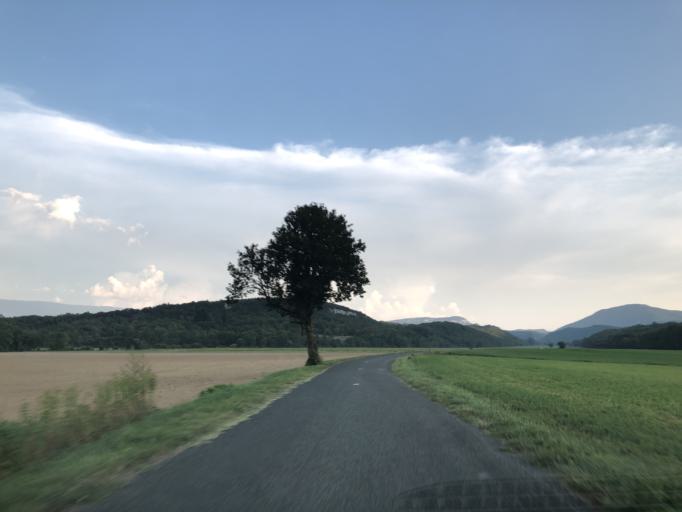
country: FR
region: Rhone-Alpes
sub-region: Departement de l'Ain
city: Belley
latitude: 45.7657
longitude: 5.6219
